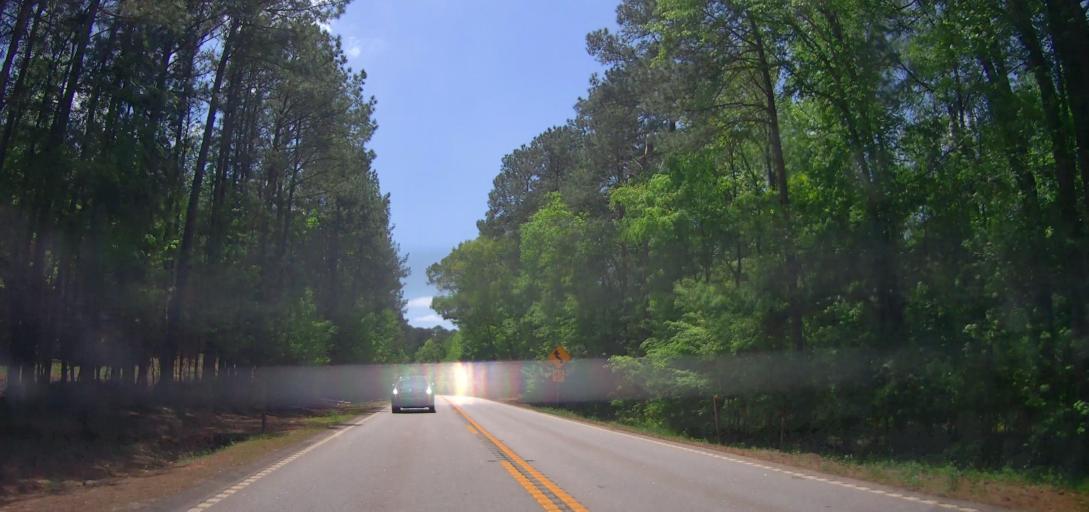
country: US
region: Georgia
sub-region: Jasper County
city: Monticello
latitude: 33.2657
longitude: -83.6755
